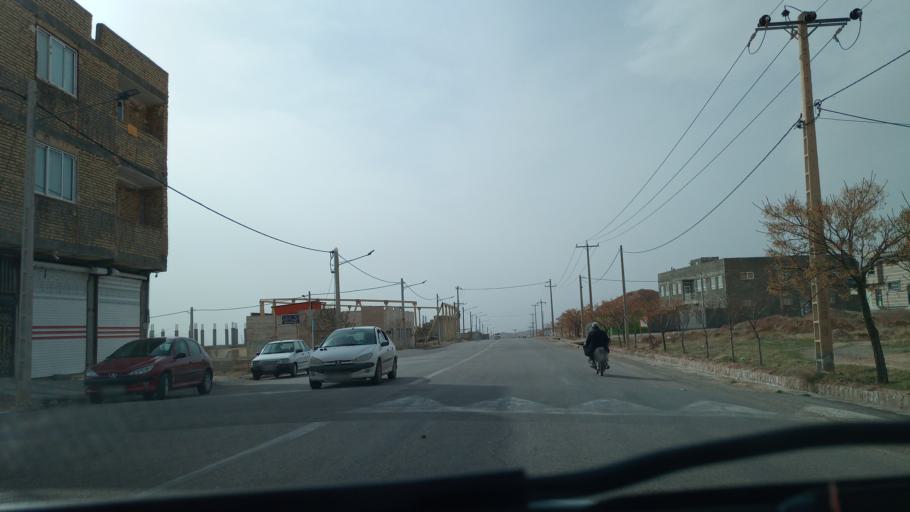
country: IR
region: Khorasan-e Shomali
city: Esfarayen
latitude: 37.0876
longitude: 57.4951
